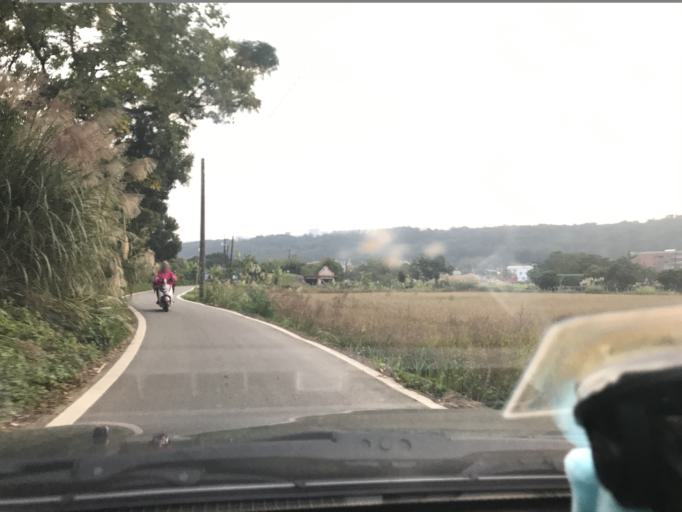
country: TW
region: Taiwan
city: Daxi
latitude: 24.8544
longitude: 121.2111
